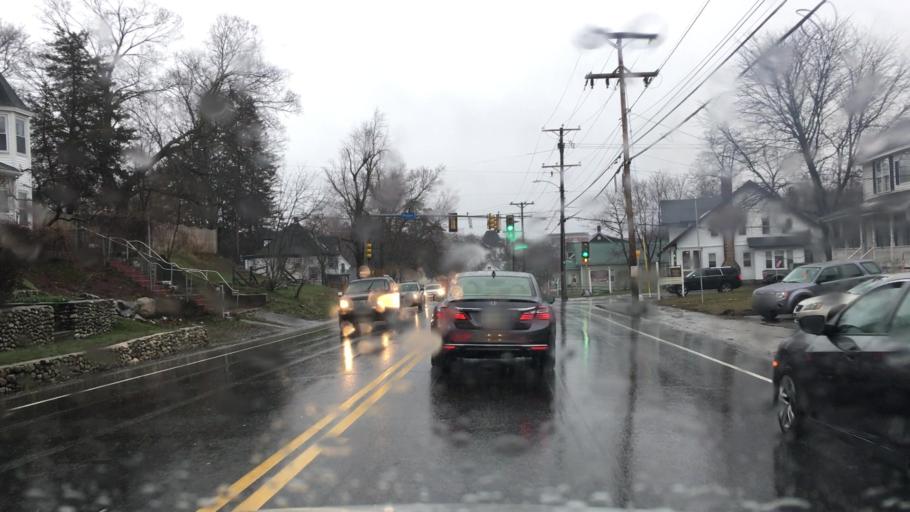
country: US
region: New Hampshire
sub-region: Rockingham County
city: Derry
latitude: 42.8771
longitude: -71.3325
